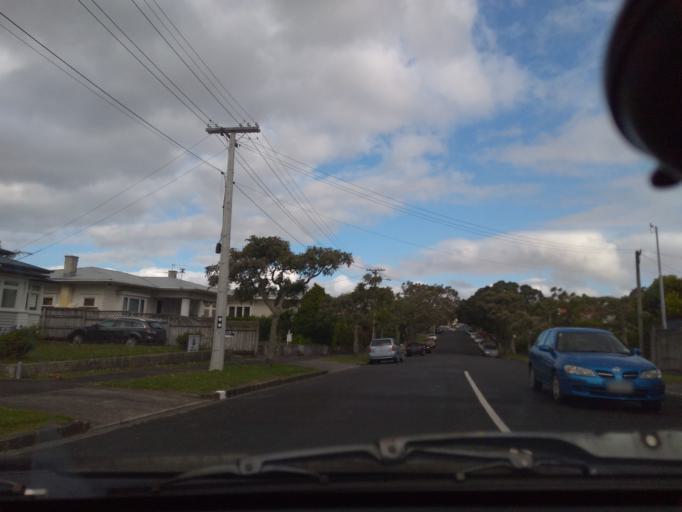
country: NZ
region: Auckland
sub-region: Auckland
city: Rosebank
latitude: -36.8756
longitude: 174.7168
